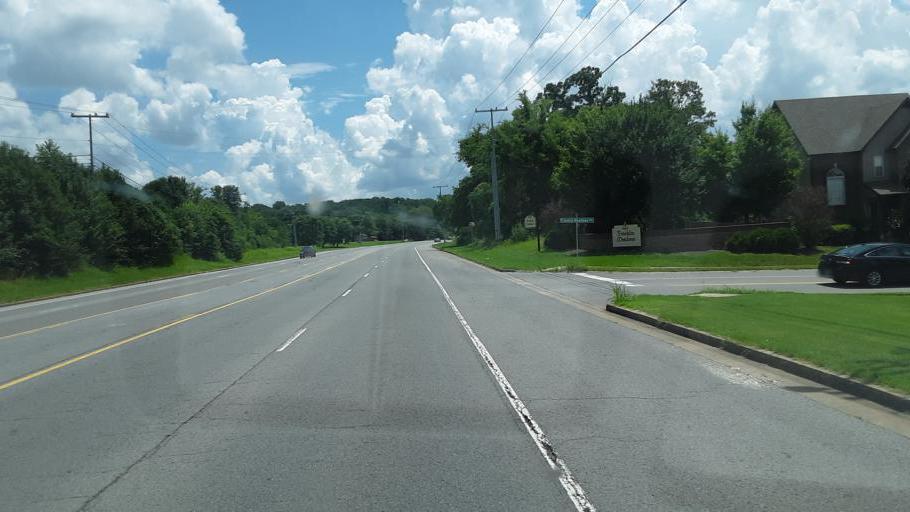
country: US
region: Kentucky
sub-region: Christian County
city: Oak Grove
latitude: 36.6298
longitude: -87.3784
